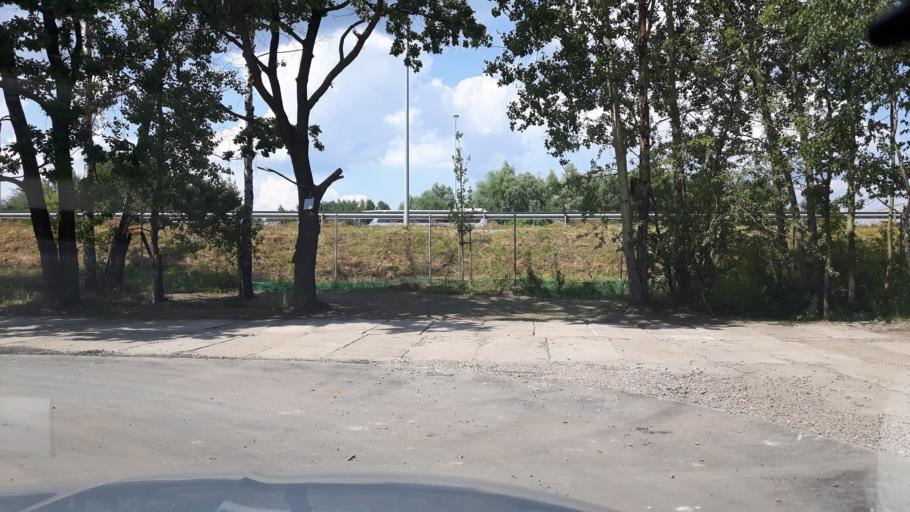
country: PL
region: Masovian Voivodeship
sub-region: Powiat wolominski
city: Marki
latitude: 52.3089
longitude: 21.1148
